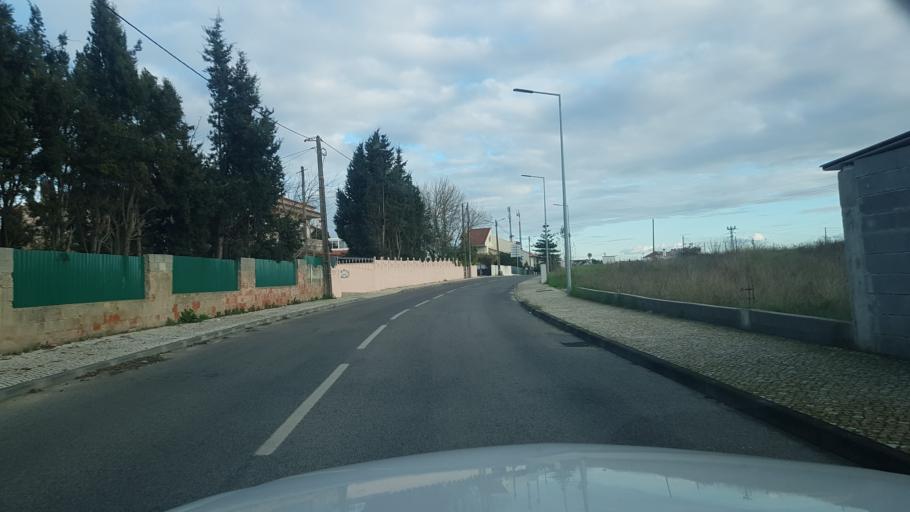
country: PT
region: Santarem
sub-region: Entroncamento
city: Entroncamento
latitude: 39.4689
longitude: -8.4844
